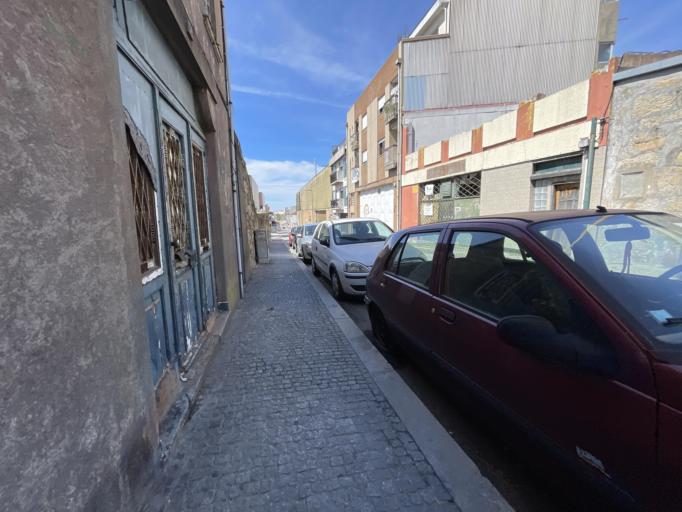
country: PT
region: Porto
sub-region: Vila Nova de Gaia
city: Vila Nova de Gaia
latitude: 41.1255
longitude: -8.6184
